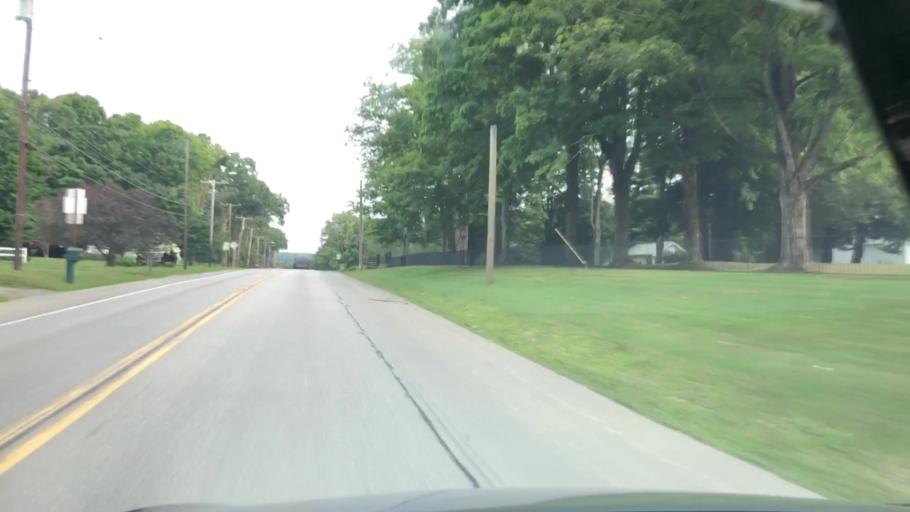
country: US
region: Pennsylvania
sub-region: Crawford County
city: Titusville
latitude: 41.6452
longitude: -79.7152
